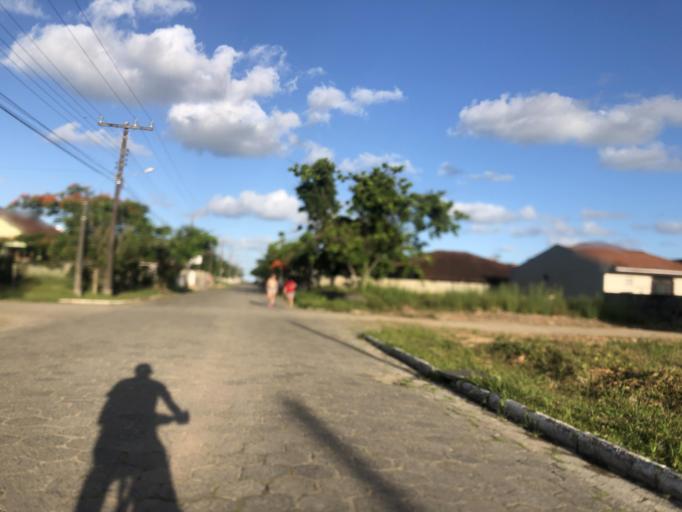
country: BR
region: Santa Catarina
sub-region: Sao Francisco Do Sul
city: Sao Francisco do Sul
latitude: -26.2175
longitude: -48.5280
